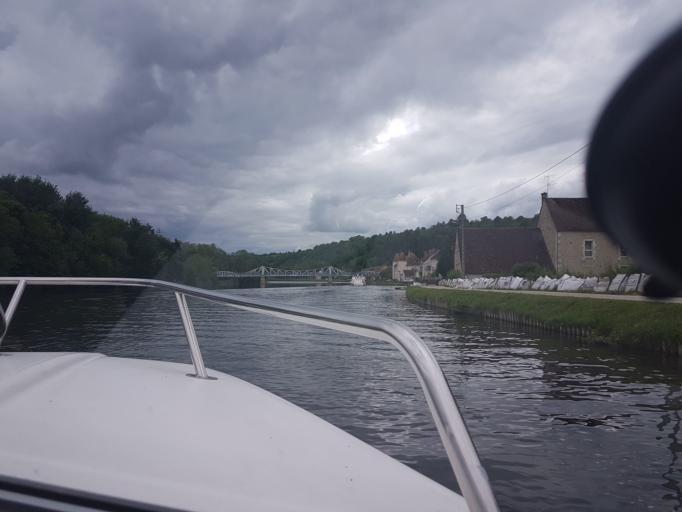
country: FR
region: Bourgogne
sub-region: Departement de l'Yonne
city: Augy
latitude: 47.7566
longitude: 3.5930
